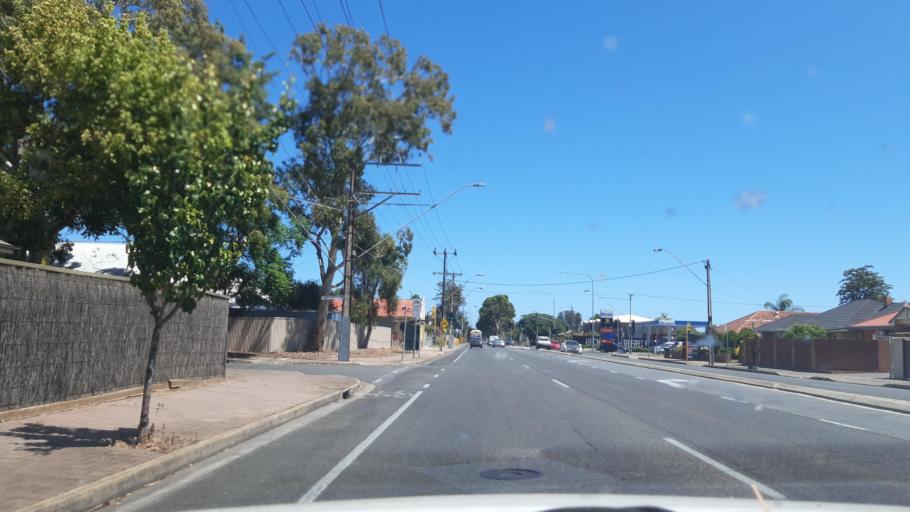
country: AU
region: South Australia
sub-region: Marion
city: South Plympton
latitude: -34.9677
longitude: 138.5651
